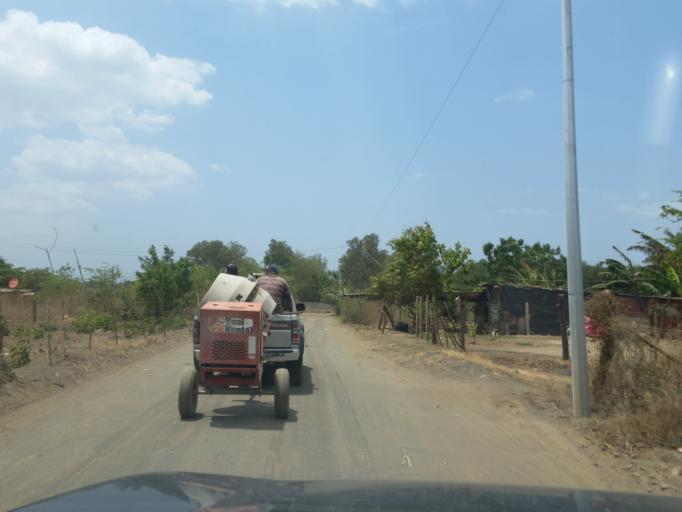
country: NI
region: Managua
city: Managua
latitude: 12.1271
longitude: -86.1629
